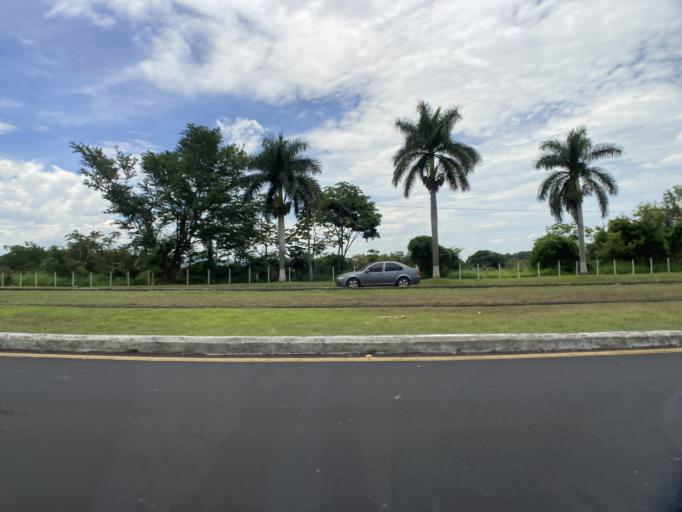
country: GT
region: Escuintla
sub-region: Municipio de Escuintla
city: Escuintla
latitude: 14.3398
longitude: -90.7937
